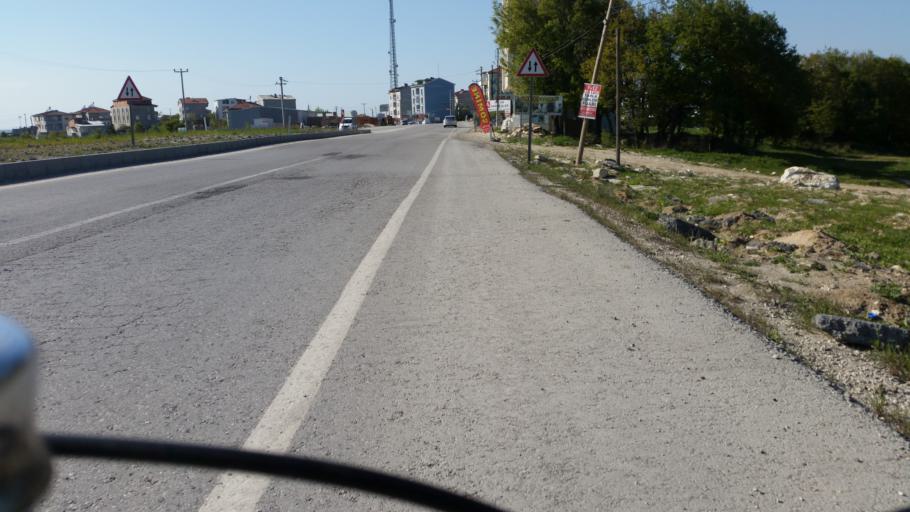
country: TR
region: Tekirdag
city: Cerkezkoey
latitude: 41.3544
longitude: 27.9554
